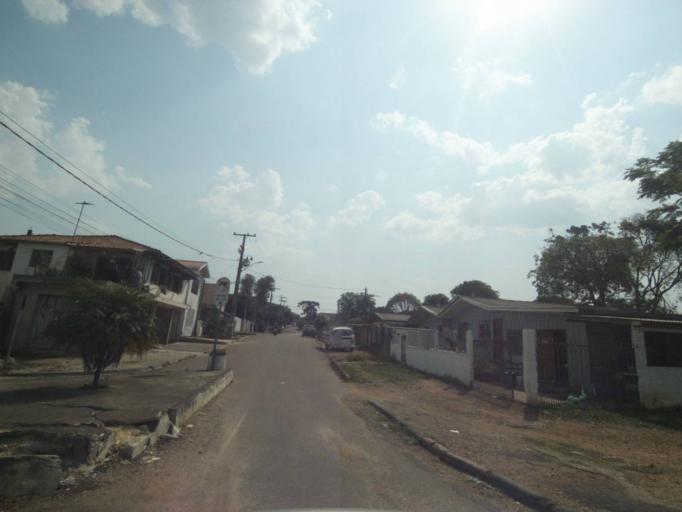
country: BR
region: Parana
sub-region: Sao Jose Dos Pinhais
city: Sao Jose dos Pinhais
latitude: -25.5414
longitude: -49.2404
